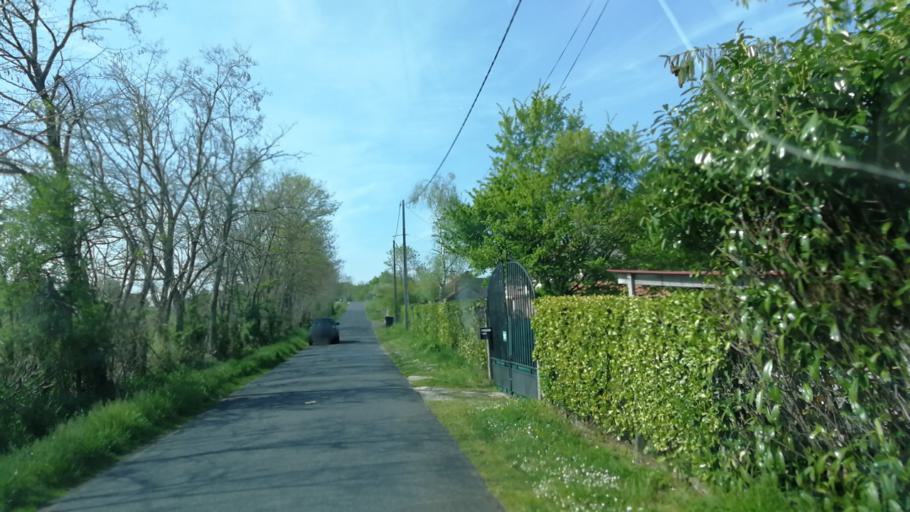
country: FR
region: Auvergne
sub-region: Departement de l'Allier
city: Neuilly-le-Real
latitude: 46.4575
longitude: 3.5444
